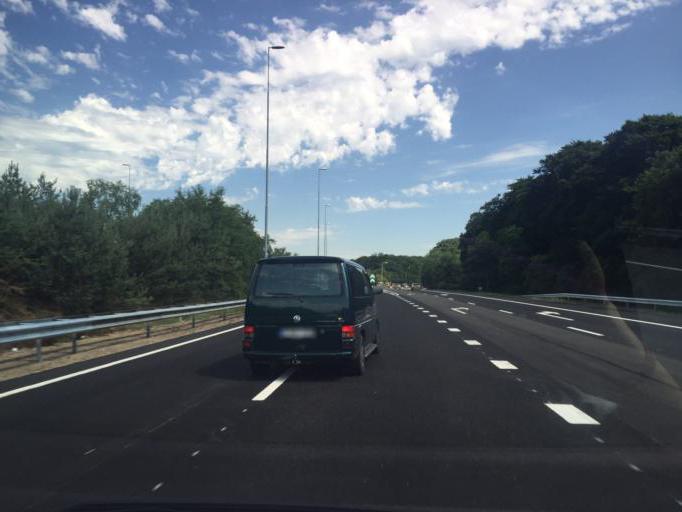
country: NL
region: Gelderland
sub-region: Gemeente Renkum
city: Wolfheze
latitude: 52.0197
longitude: 5.8184
